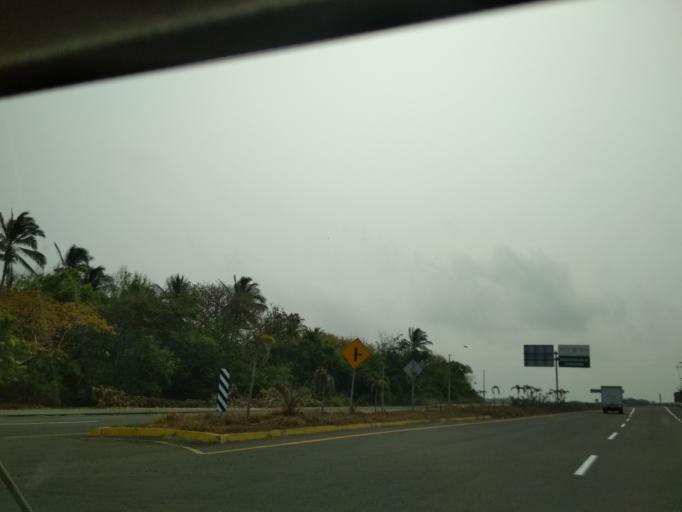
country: MX
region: Veracruz
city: Anton Lizardo
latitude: 19.0511
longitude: -96.0111
